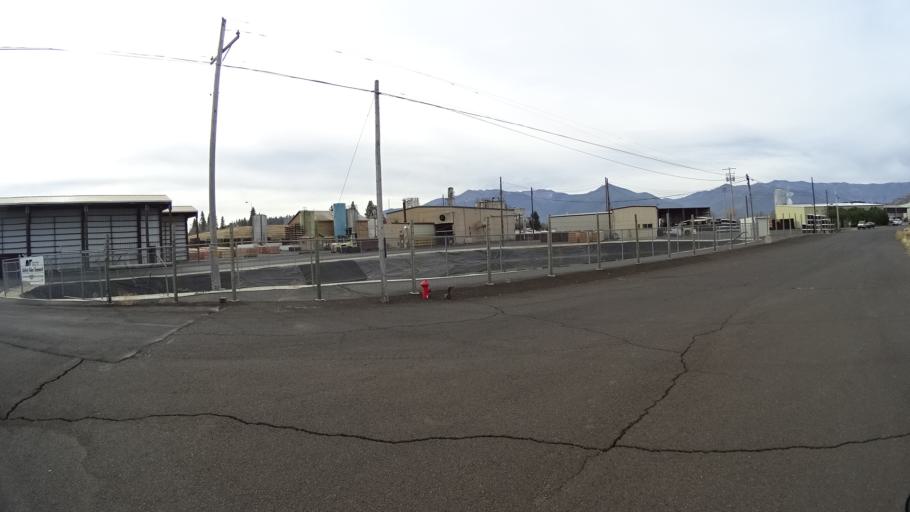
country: US
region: California
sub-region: Siskiyou County
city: Weed
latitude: 41.4341
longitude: -122.3731
